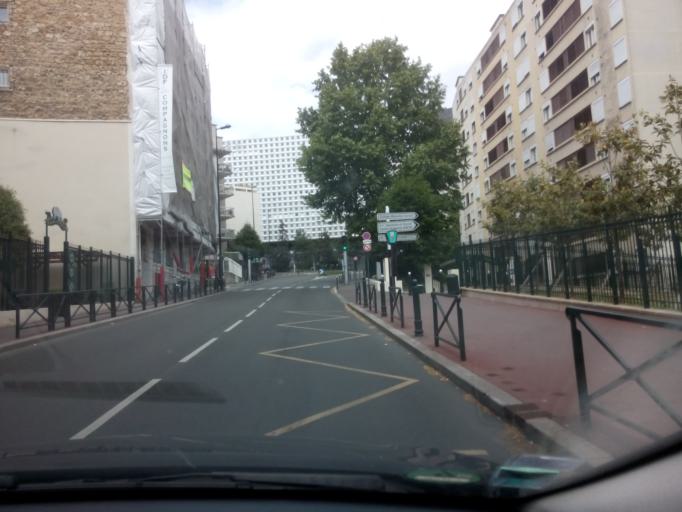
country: FR
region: Ile-de-France
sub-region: Departement des Hauts-de-Seine
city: Puteaux
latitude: 48.8849
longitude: 2.2394
